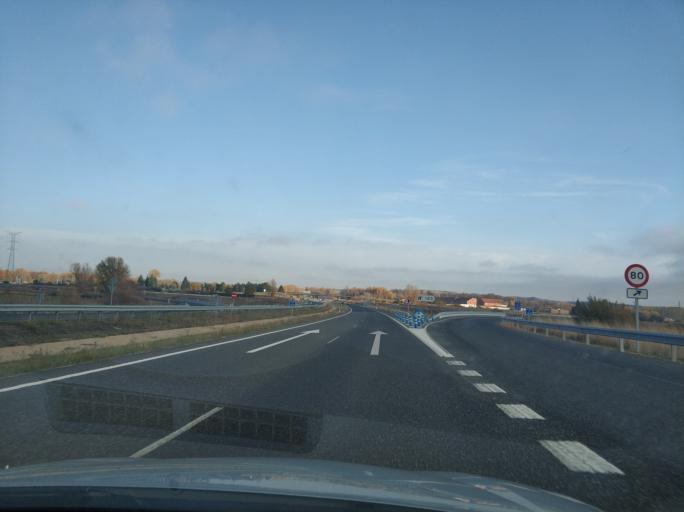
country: ES
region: Castille and Leon
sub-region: Provincia de Leon
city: Villaturiel
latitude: 42.5534
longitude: -5.4622
